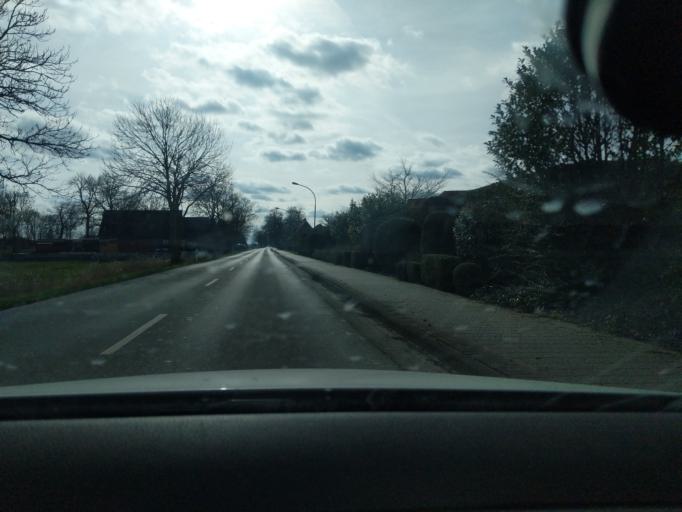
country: DE
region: Lower Saxony
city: Drochtersen
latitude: 53.6965
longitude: 9.4090
